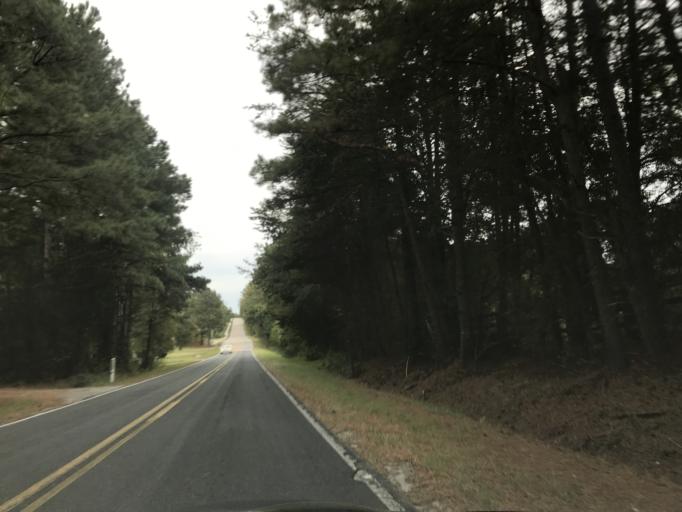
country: US
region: North Carolina
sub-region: Wake County
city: Knightdale
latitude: 35.8189
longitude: -78.4861
